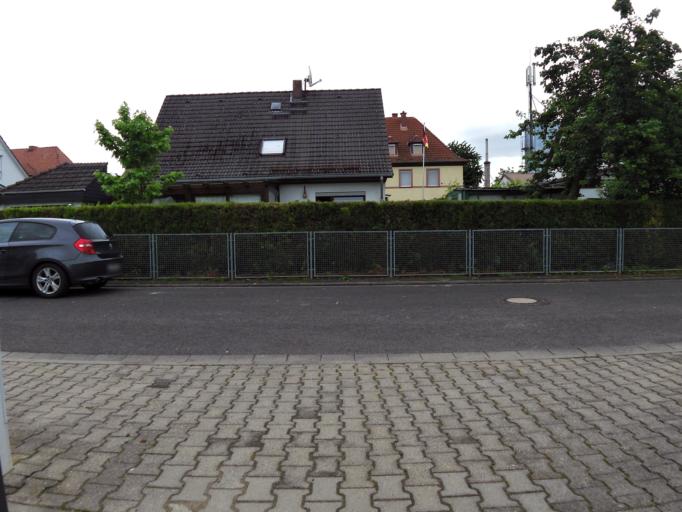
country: DE
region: Rheinland-Pfalz
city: Dirmstein
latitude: 49.5688
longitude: 8.2484
